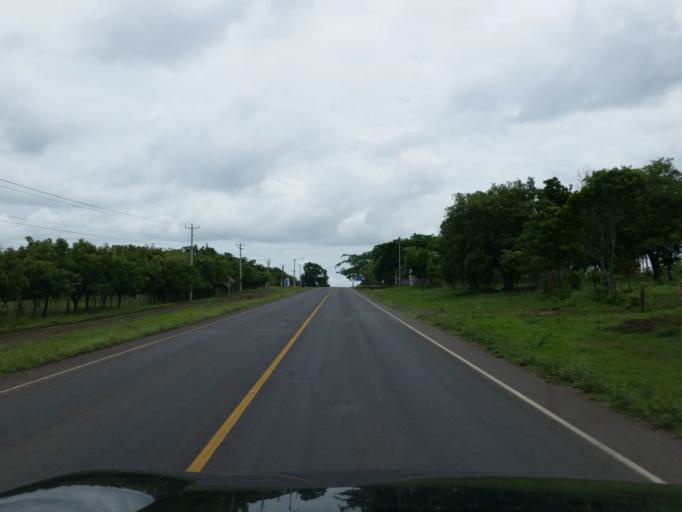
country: NI
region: Managua
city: Tipitapa
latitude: 12.3537
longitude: -86.0491
